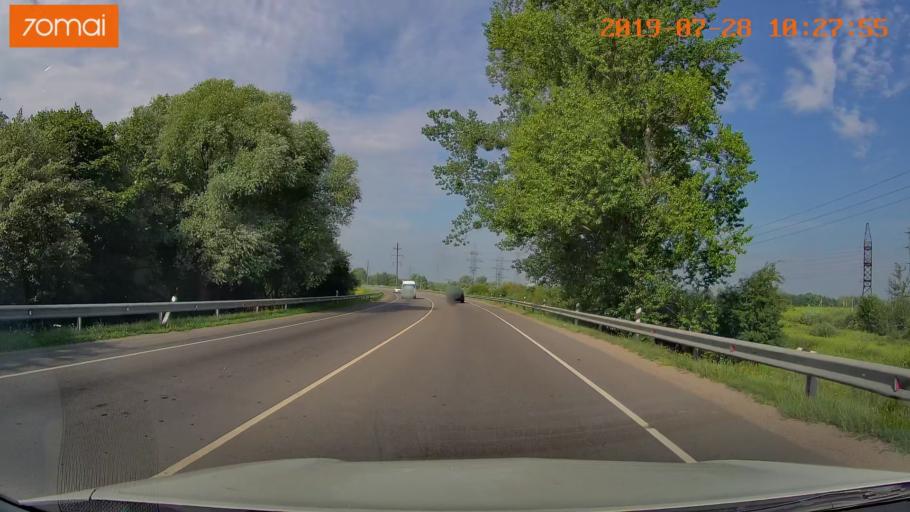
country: RU
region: Kaliningrad
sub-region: Gorod Kaliningrad
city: Kaliningrad
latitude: 54.7717
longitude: 20.5083
